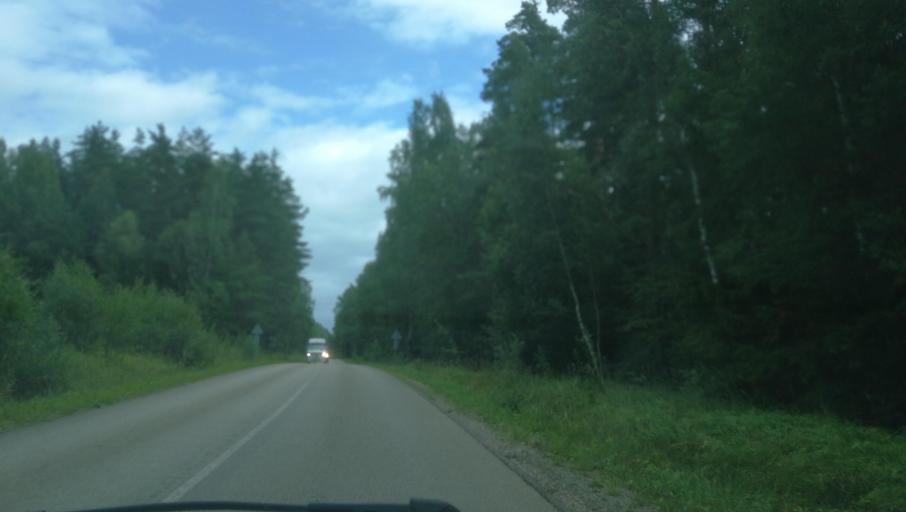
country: LV
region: Priekuli
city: Priekuli
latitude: 57.3650
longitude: 25.3821
